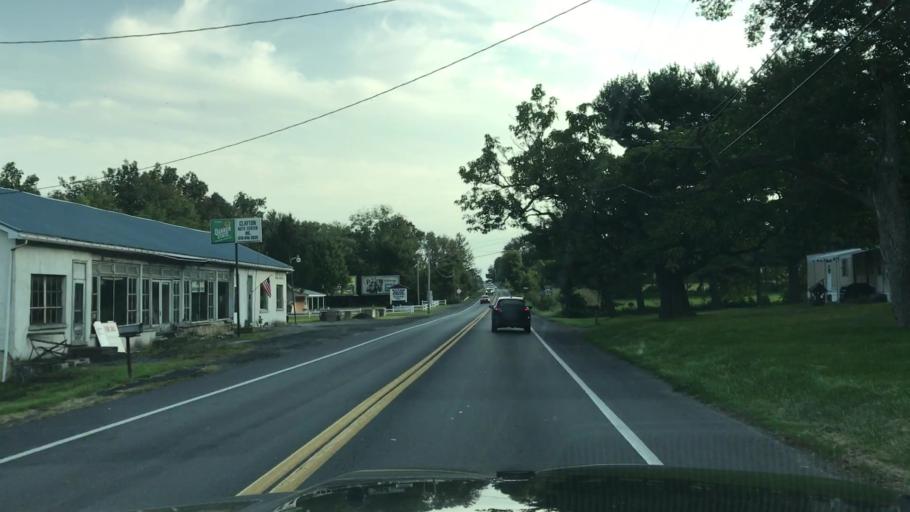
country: US
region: Pennsylvania
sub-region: Berks County
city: Bally
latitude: 40.4174
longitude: -75.5740
